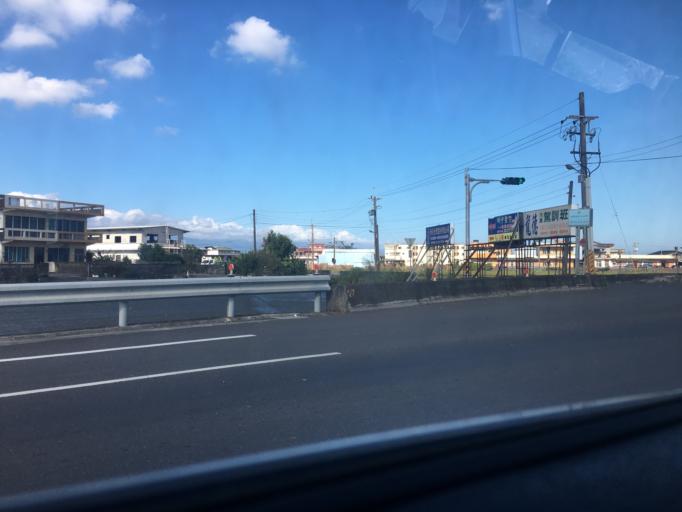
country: TW
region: Taiwan
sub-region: Yilan
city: Yilan
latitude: 24.7025
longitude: 121.7484
